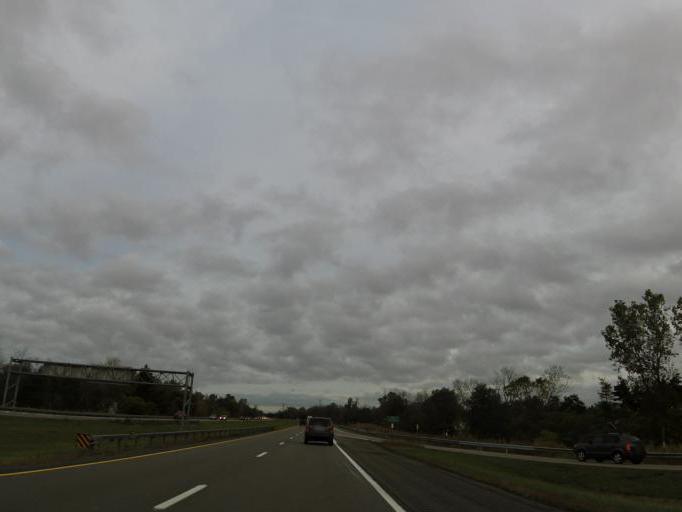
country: US
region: New York
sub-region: Erie County
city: Elma Center
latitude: 42.8360
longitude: -78.7006
